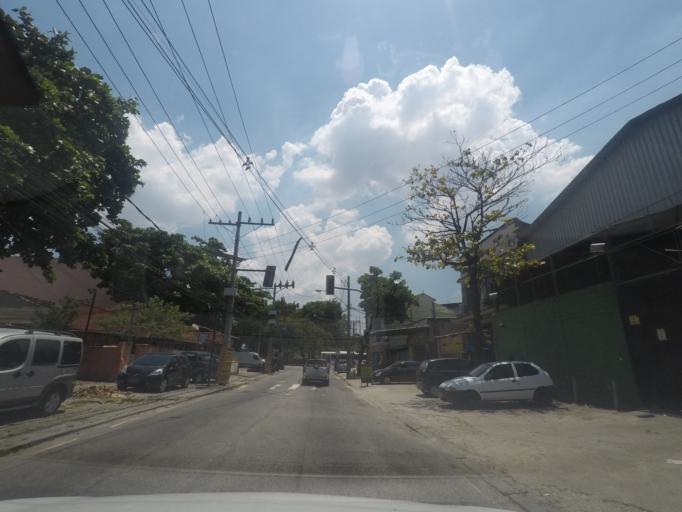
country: BR
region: Rio de Janeiro
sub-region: Duque De Caxias
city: Duque de Caxias
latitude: -22.8233
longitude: -43.3082
